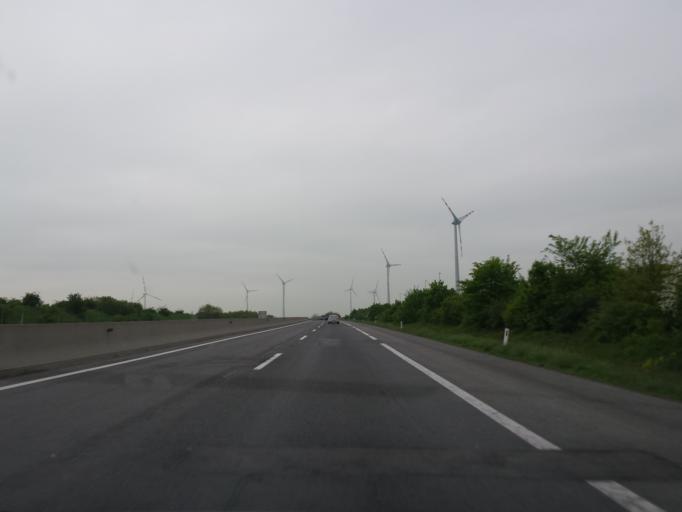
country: AT
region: Burgenland
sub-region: Politischer Bezirk Neusiedl am See
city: Zurndorf
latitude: 47.9327
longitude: 16.9937
